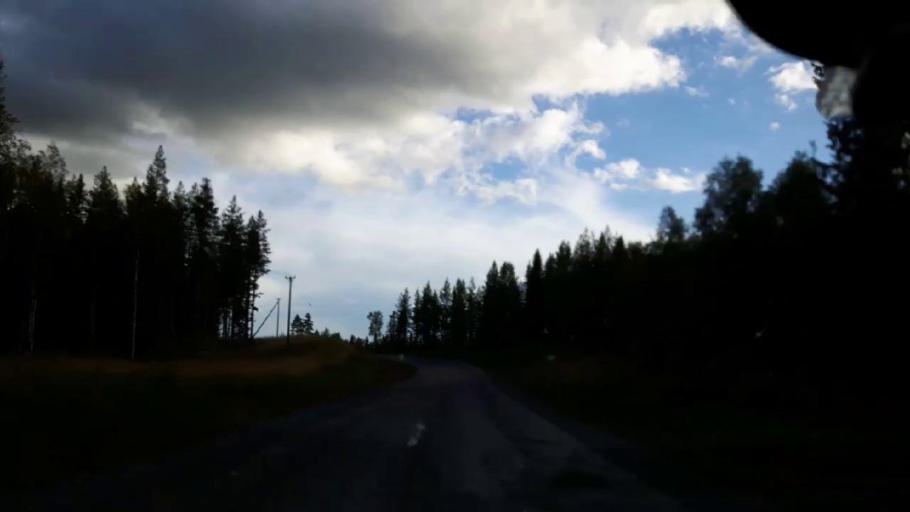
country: SE
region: Jaemtland
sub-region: Stroemsunds Kommun
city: Stroemsund
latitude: 63.3225
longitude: 15.5832
